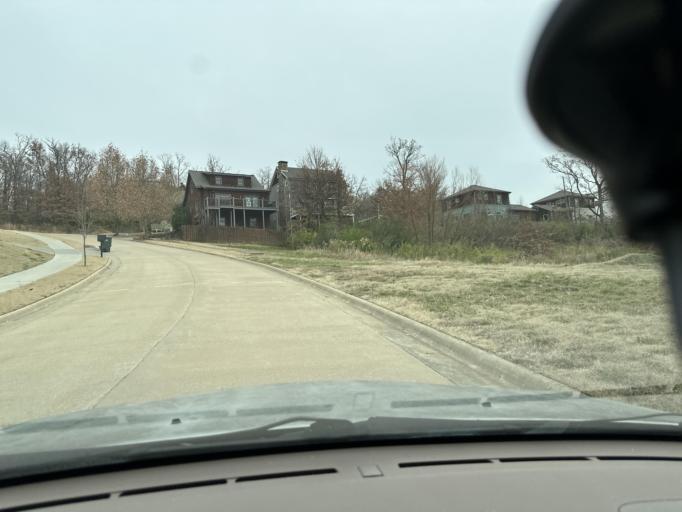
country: US
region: Arkansas
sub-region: Washington County
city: Fayetteville
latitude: 36.0942
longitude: -94.1511
